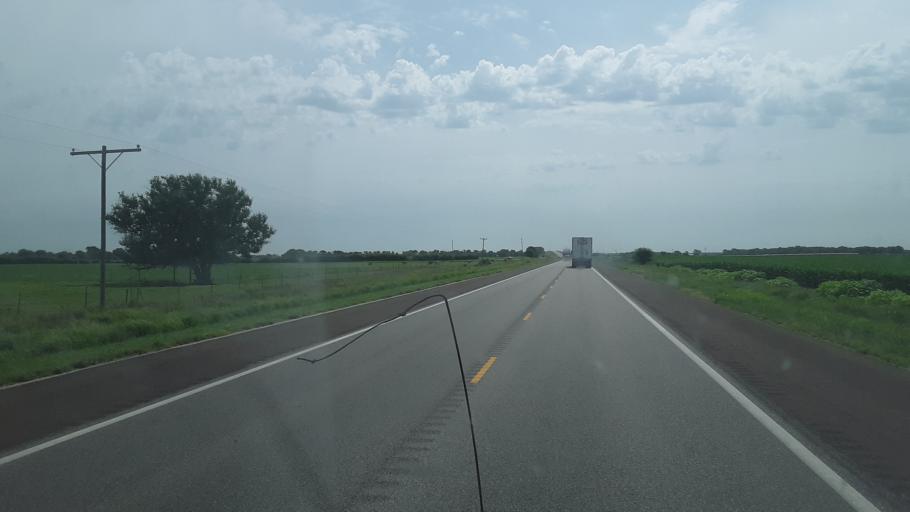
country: US
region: Kansas
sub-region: Reno County
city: South Hutchinson
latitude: 37.9845
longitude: -98.0726
